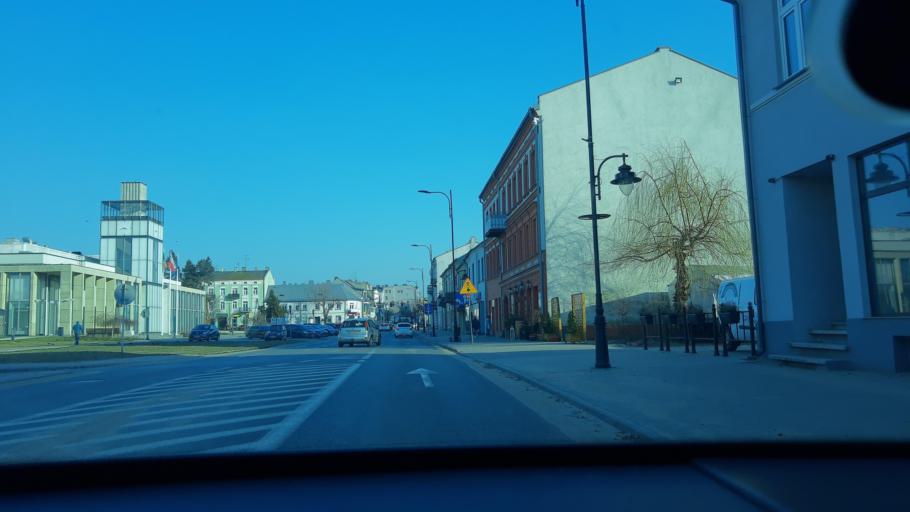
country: PL
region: Lodz Voivodeship
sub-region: Powiat zdunskowolski
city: Zdunska Wola
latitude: 51.6028
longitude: 18.9316
